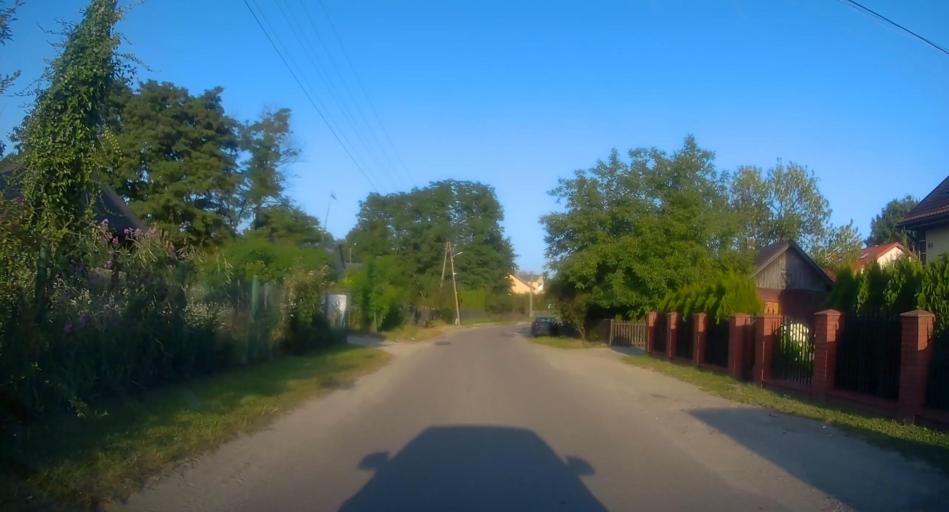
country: PL
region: Lodz Voivodeship
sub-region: Powiat skierniewicki
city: Kowiesy
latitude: 51.9011
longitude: 20.3682
